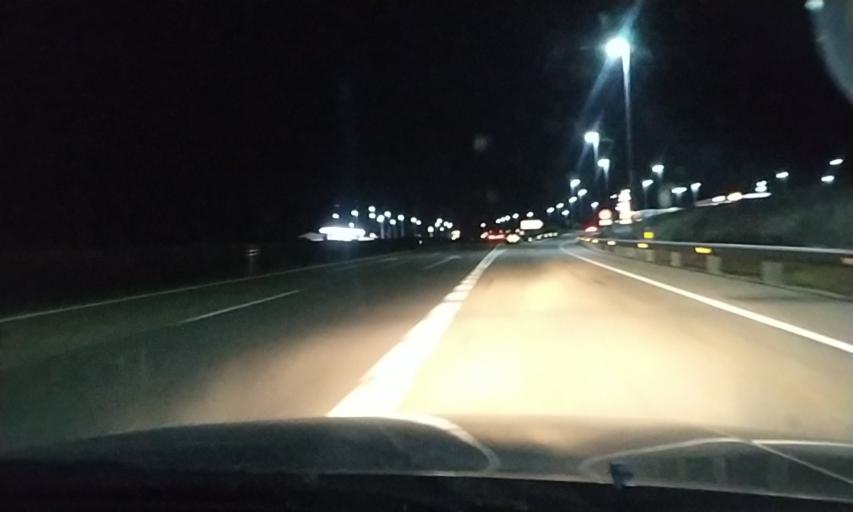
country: ES
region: Castille and Leon
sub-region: Provincia de Zamora
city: Pobladura del Valle
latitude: 42.0911
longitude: -5.7154
